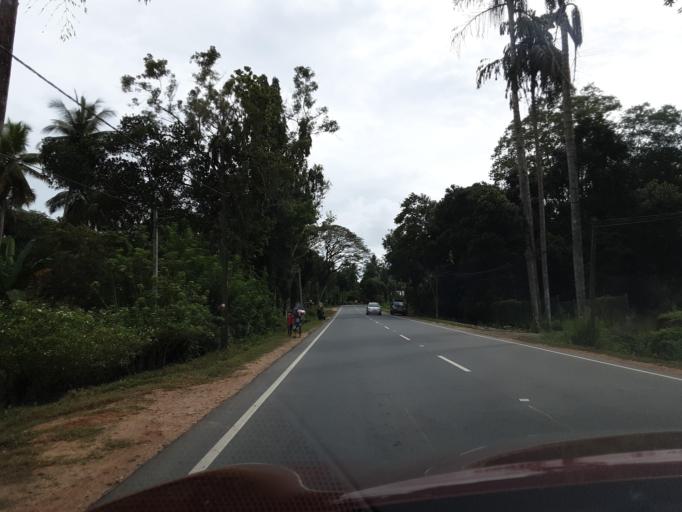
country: LK
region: Eastern Province
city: Eravur Town
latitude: 7.5185
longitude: 81.3435
